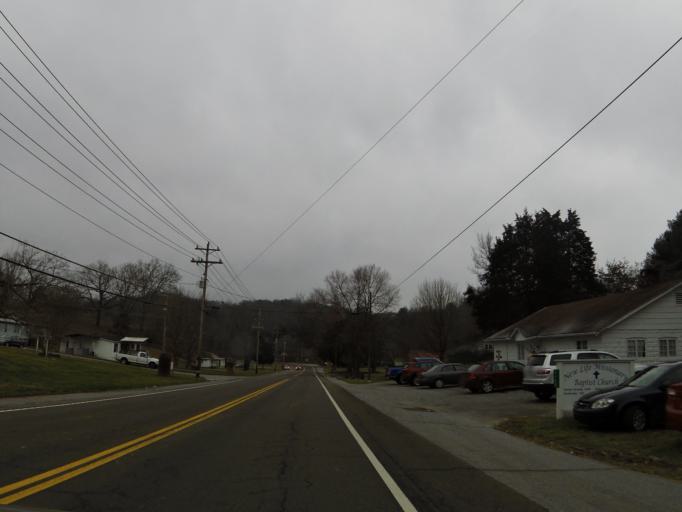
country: US
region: Tennessee
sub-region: Anderson County
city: Clinton
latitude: 36.1257
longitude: -84.1448
